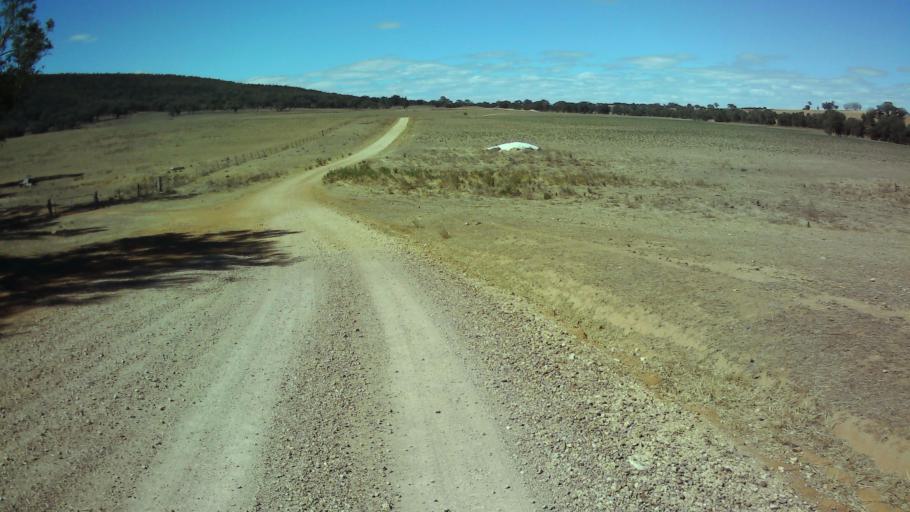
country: AU
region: New South Wales
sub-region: Weddin
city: Grenfell
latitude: -34.0349
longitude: 148.4342
